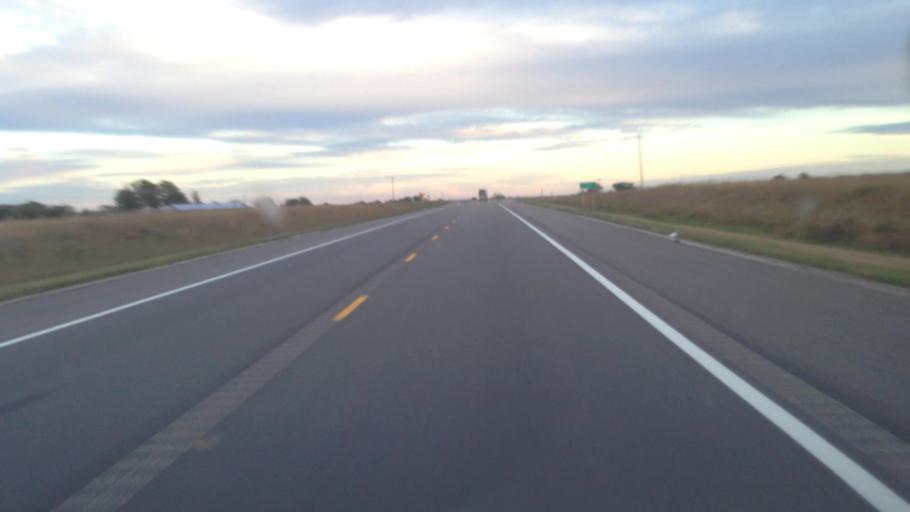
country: US
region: Kansas
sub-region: Franklin County
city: Ottawa
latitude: 38.4646
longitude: -95.2552
